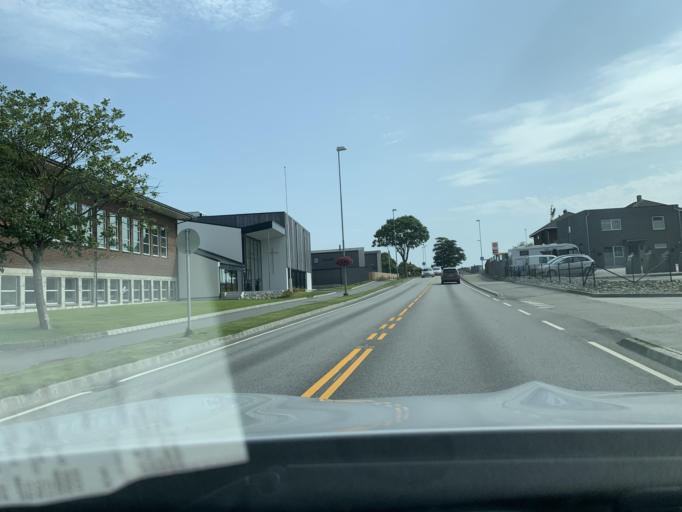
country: NO
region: Rogaland
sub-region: Klepp
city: Kleppe
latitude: 58.7719
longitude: 5.6299
